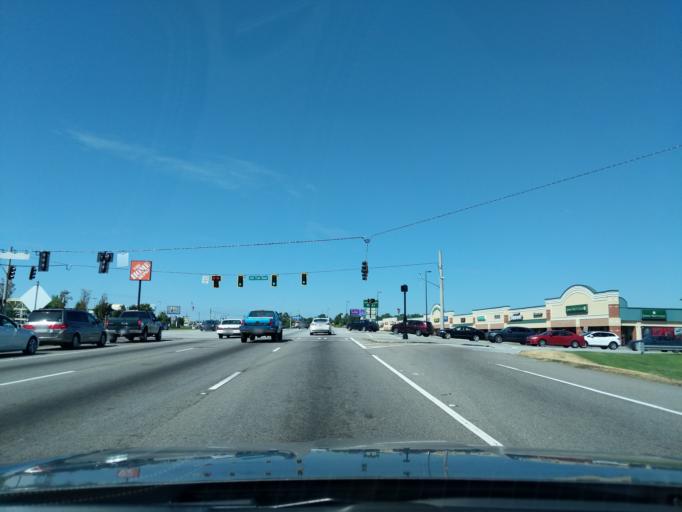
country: US
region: Georgia
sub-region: Columbia County
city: Martinez
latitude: 33.5008
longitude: -82.0871
